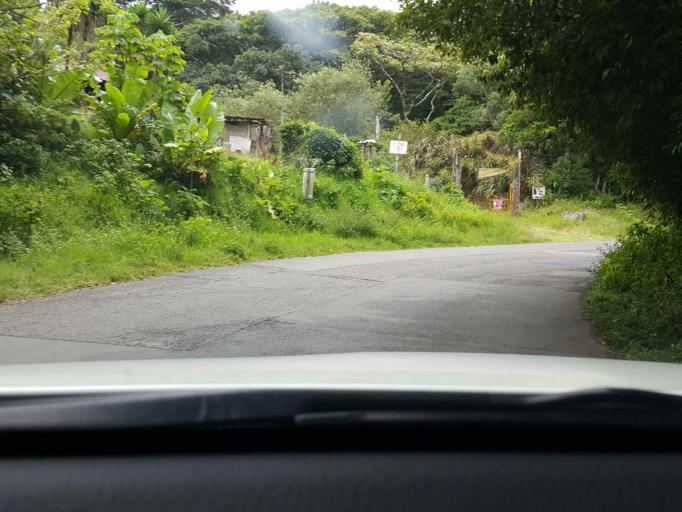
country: CR
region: Heredia
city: San Josecito
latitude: 10.0580
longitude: -84.0895
